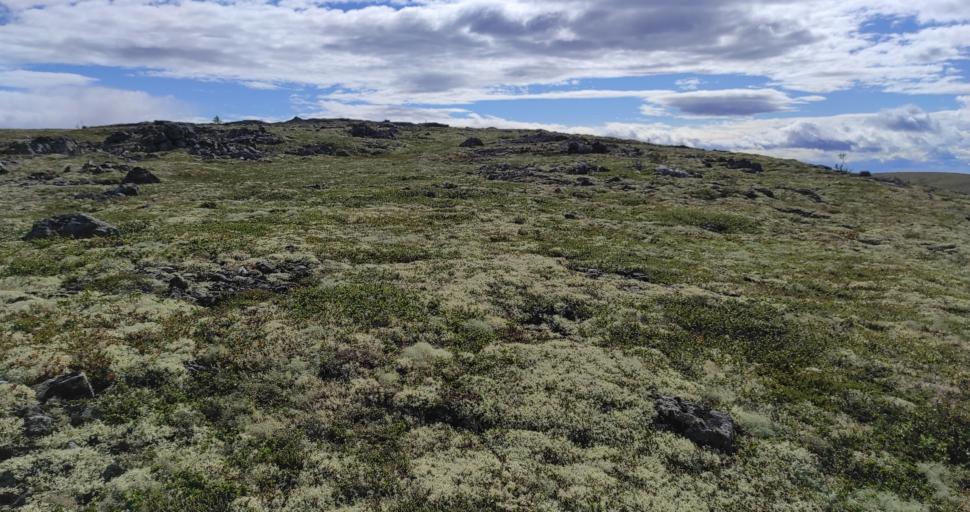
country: RU
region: Murmansk
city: Afrikanda
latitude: 67.0462
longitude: 32.9522
